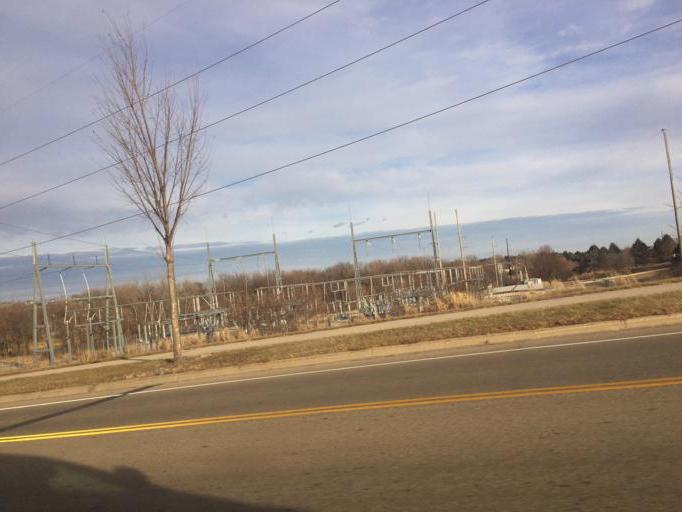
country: US
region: Minnesota
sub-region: Olmsted County
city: Oronoco
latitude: 44.0800
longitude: -92.5388
